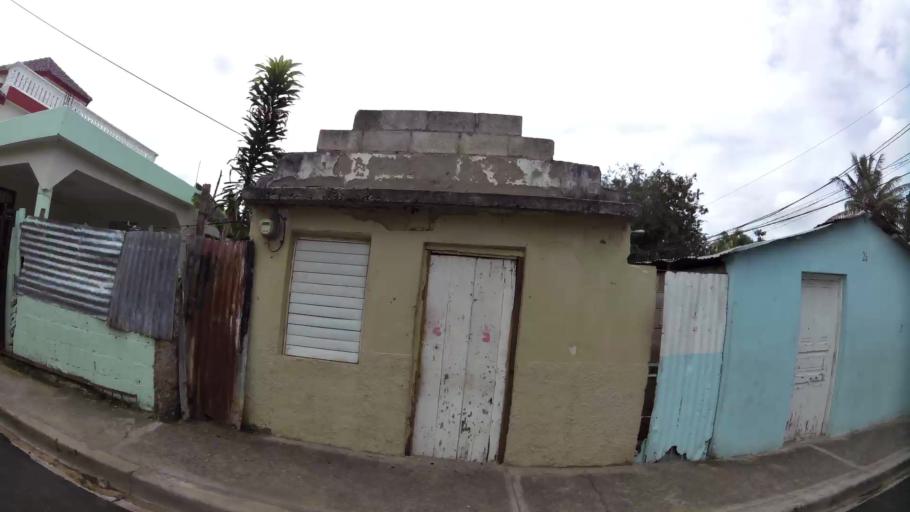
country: DO
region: Santiago
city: Santiago de los Caballeros
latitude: 19.4278
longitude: -70.6708
